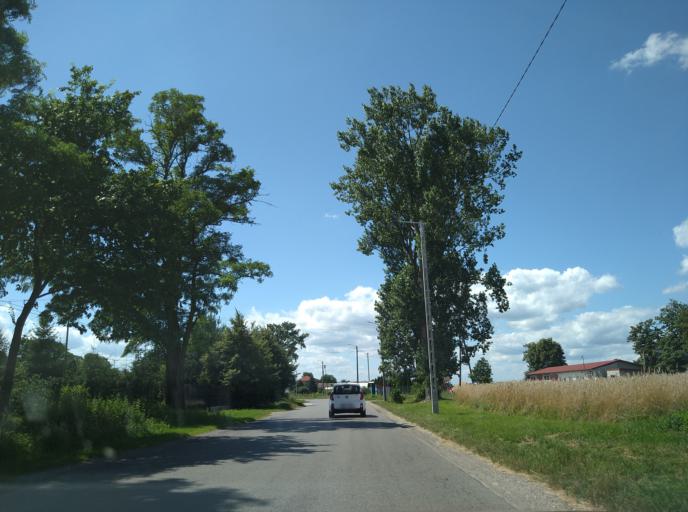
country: PL
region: Masovian Voivodeship
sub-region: Powiat bialobrzeski
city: Bialobrzegi
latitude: 51.6707
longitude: 20.8886
